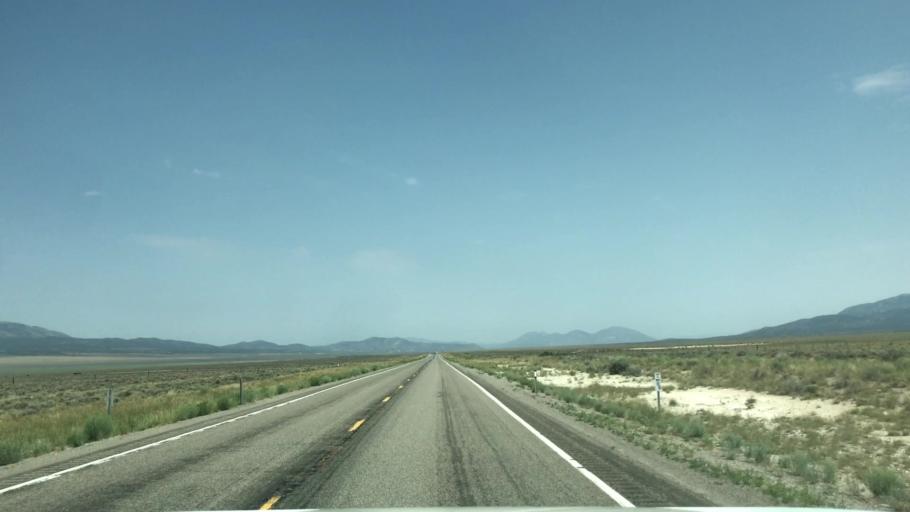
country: US
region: Nevada
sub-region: White Pine County
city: Ely
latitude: 39.0716
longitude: -114.7398
